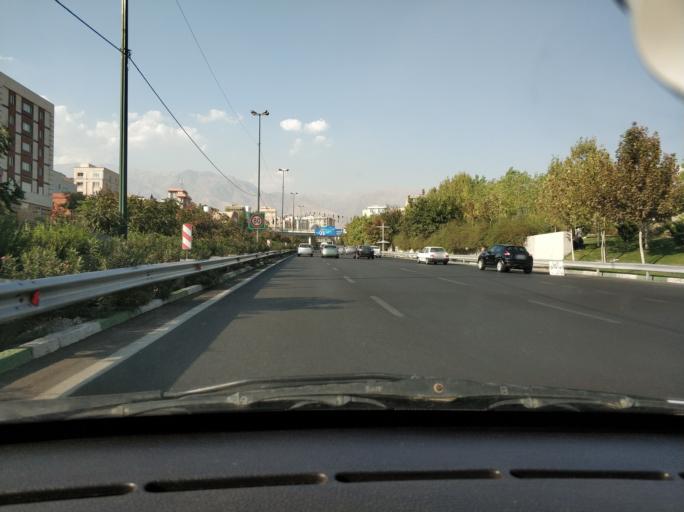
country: IR
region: Tehran
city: Tajrish
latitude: 35.7586
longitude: 51.4656
